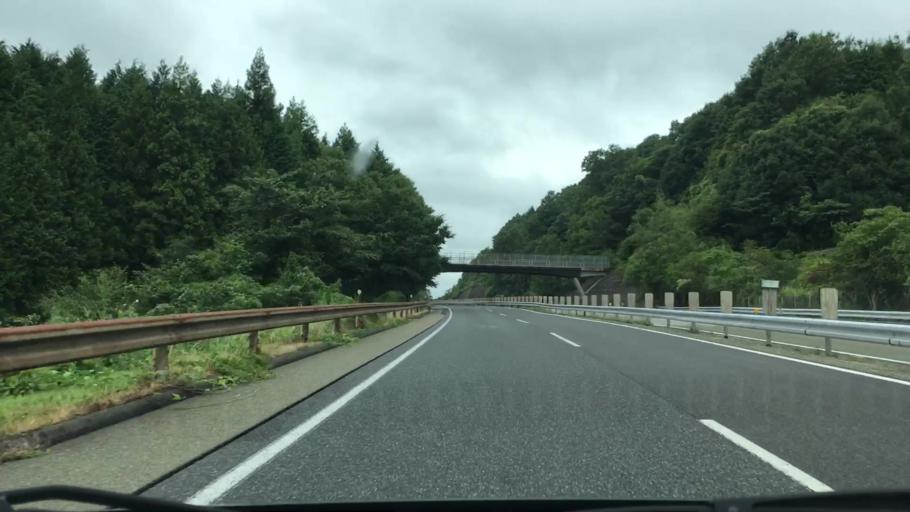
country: JP
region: Hiroshima
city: Shobara
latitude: 34.8272
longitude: 133.0570
